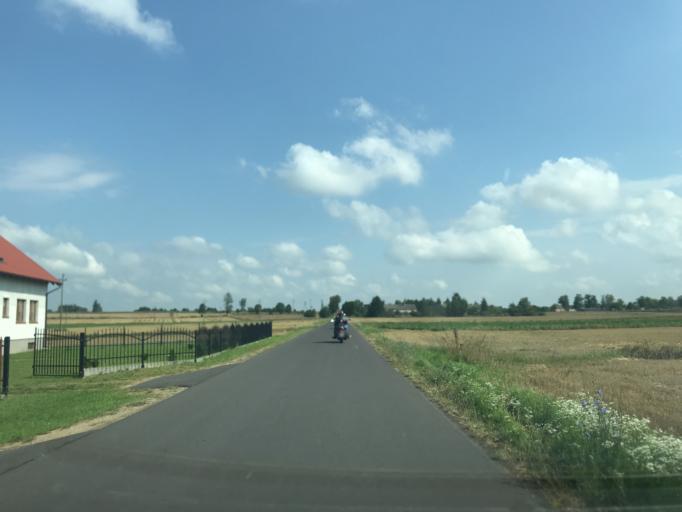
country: PL
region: Warmian-Masurian Voivodeship
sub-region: Powiat nowomiejski
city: Biskupiec
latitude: 53.4606
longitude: 19.4613
